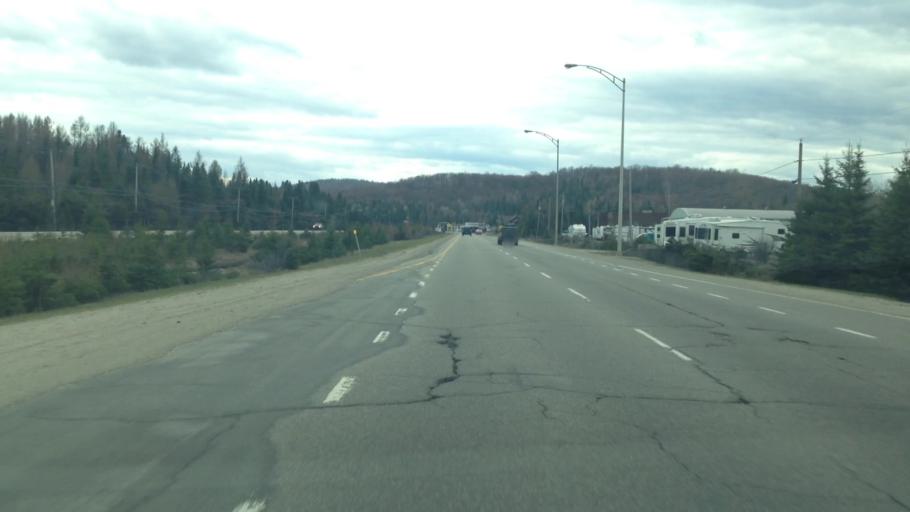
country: CA
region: Quebec
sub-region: Laurentides
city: Sainte-Agathe-des-Monts
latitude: 46.0715
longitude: -74.3141
